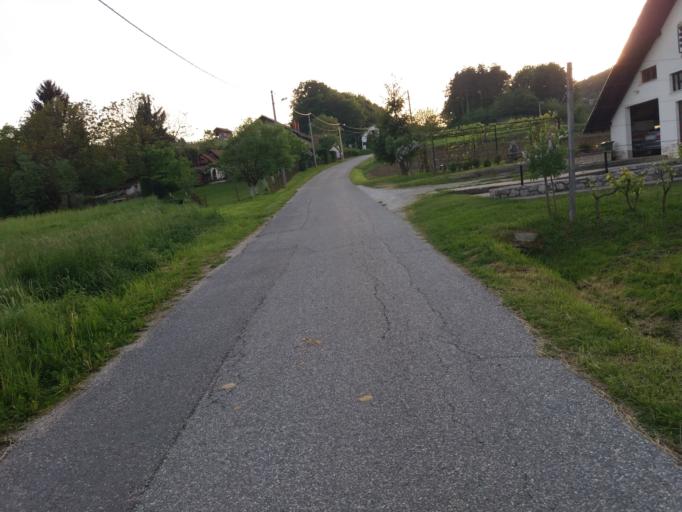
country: HR
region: Varazdinska
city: Klenovnik
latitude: 46.2464
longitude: 16.0476
